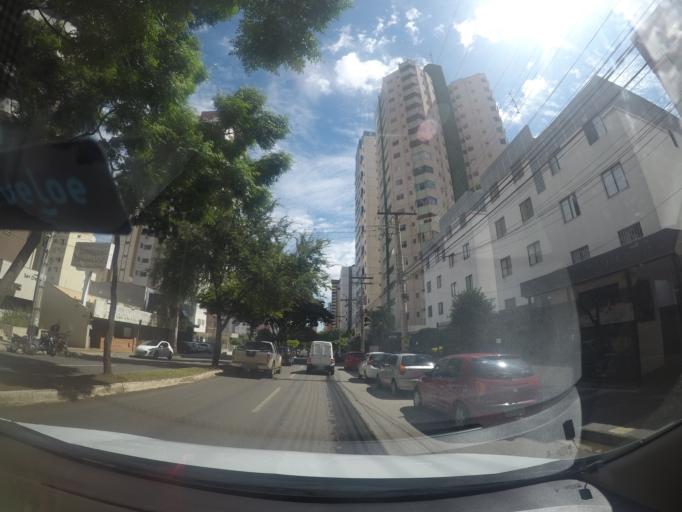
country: BR
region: Goias
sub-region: Goiania
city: Goiania
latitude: -16.7167
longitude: -49.2667
